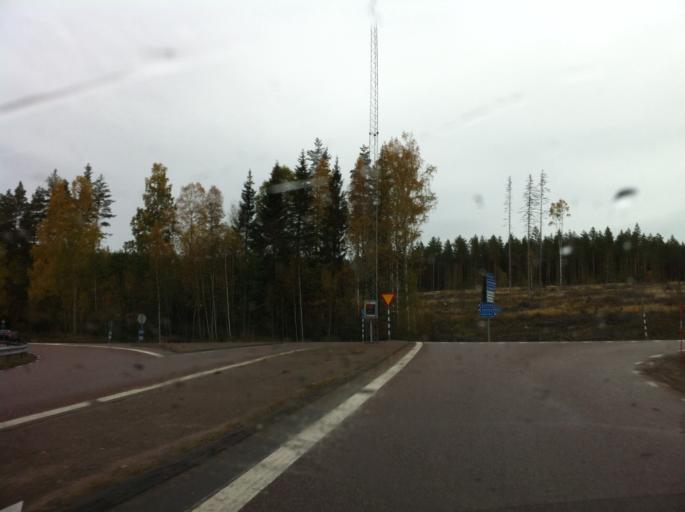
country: SE
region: Dalarna
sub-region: Ludvika Kommun
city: Grangesberg
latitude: 60.2266
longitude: 14.9830
